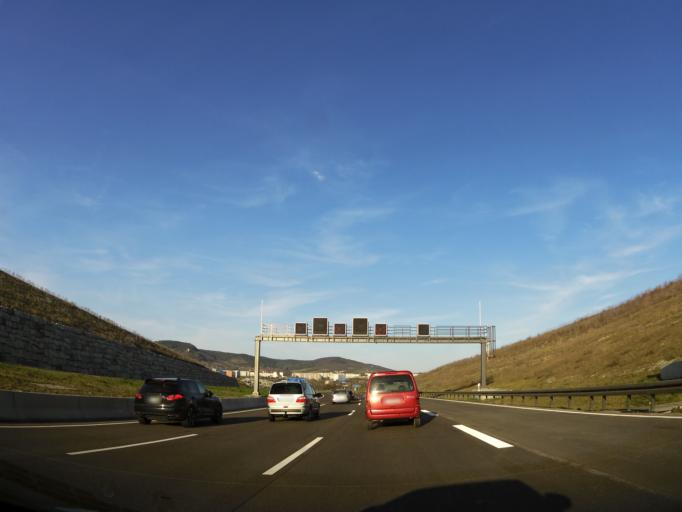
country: DE
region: Thuringia
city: Rothenstein
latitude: 50.8706
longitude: 11.5912
